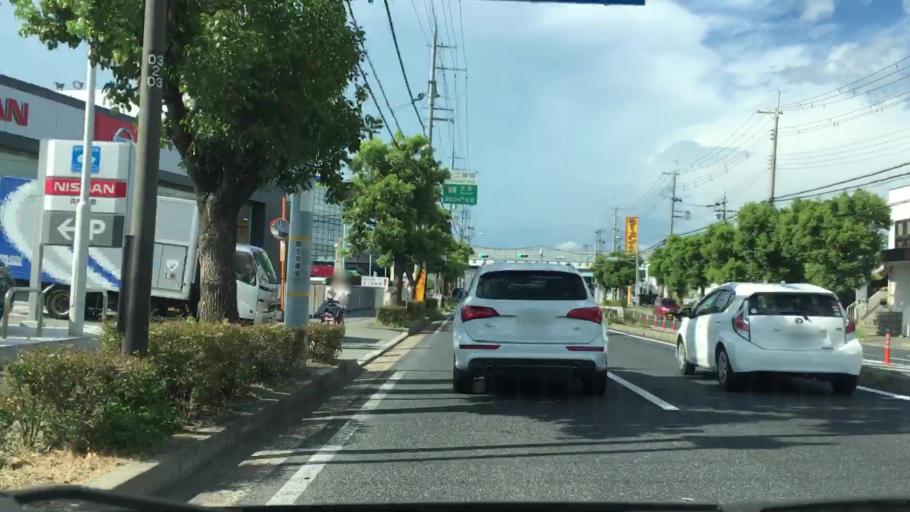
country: JP
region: Hyogo
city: Akashi
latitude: 34.6824
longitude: 134.9823
